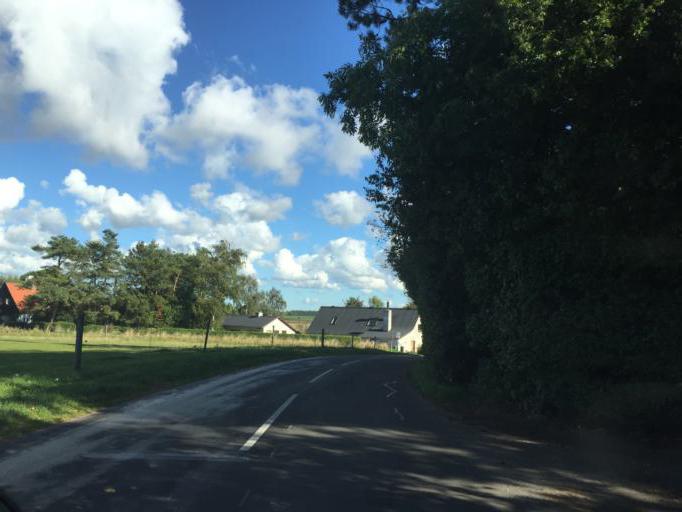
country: DK
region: Zealand
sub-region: Roskilde Kommune
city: Roskilde
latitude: 55.6787
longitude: 12.0856
